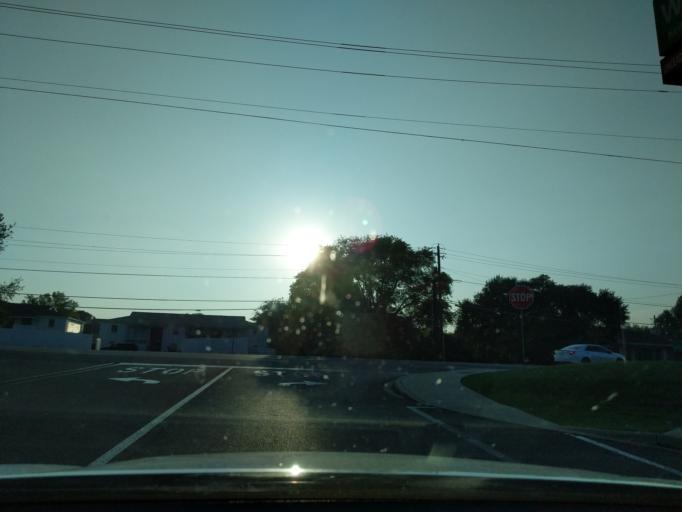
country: US
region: Alabama
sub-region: Madison County
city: Redstone Arsenal
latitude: 34.7139
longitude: -86.6267
